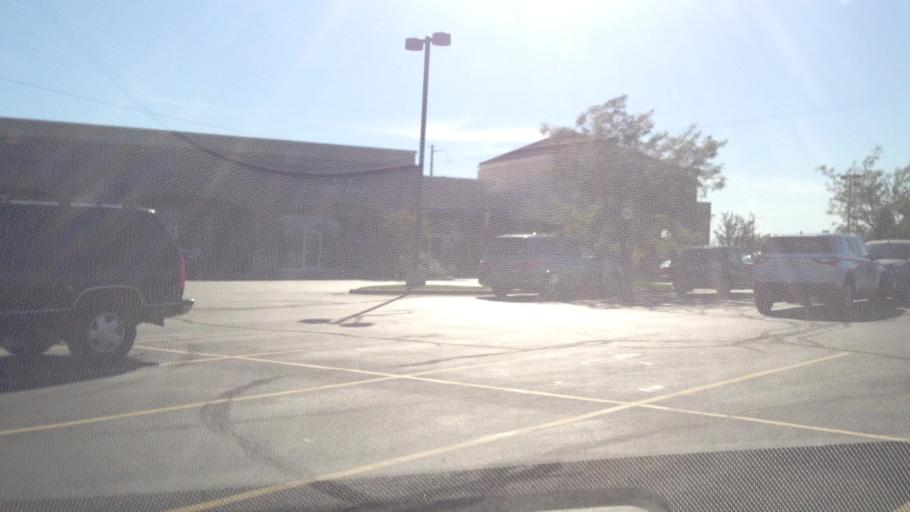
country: US
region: Kansas
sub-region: Johnson County
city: Olathe
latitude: 38.9468
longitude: -94.8173
